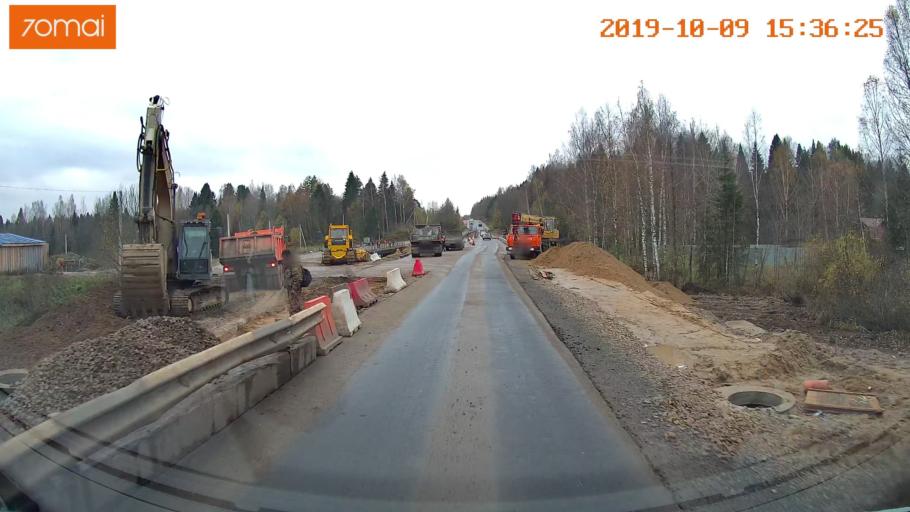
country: RU
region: Kostroma
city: Oktyabr'skiy
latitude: 57.9238
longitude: 41.2106
